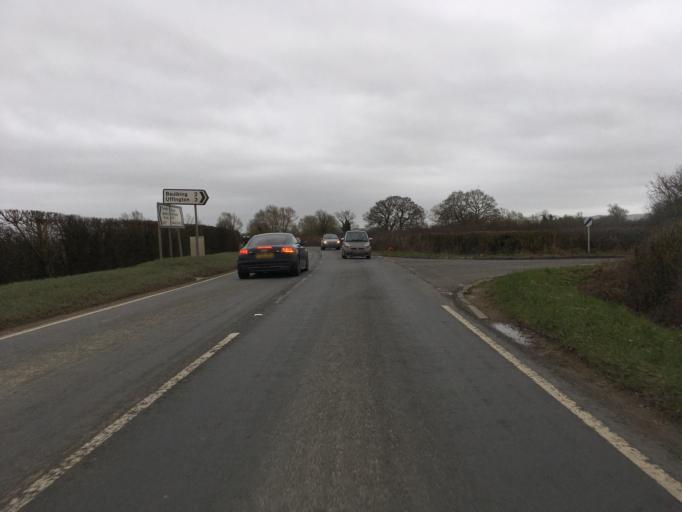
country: GB
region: England
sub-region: Oxfordshire
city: Stanford in the Vale
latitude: 51.6233
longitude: -1.5000
